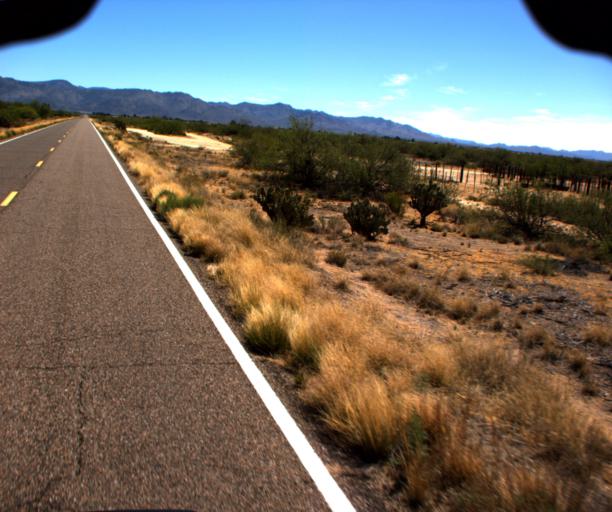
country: US
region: Arizona
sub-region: Yavapai County
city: Congress
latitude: 34.1524
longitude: -112.8775
